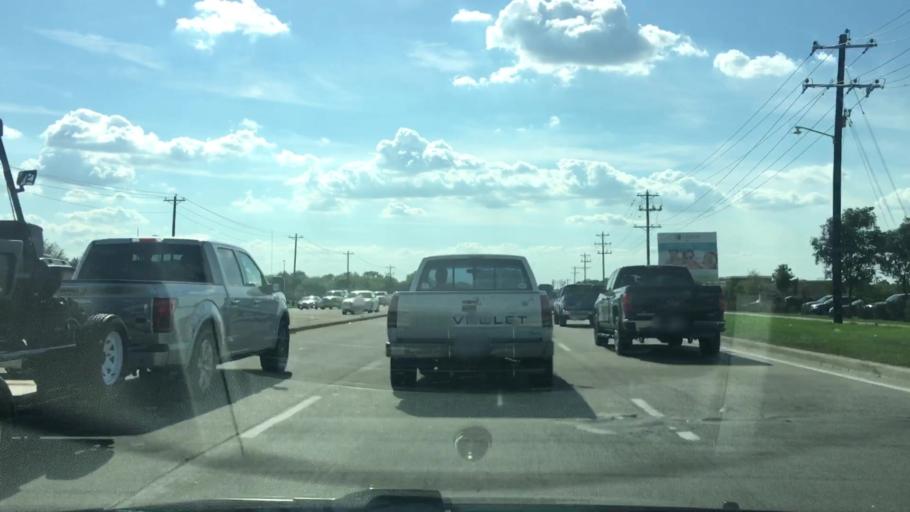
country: US
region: Texas
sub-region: Collin County
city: Prosper
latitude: 33.2186
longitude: -96.7331
